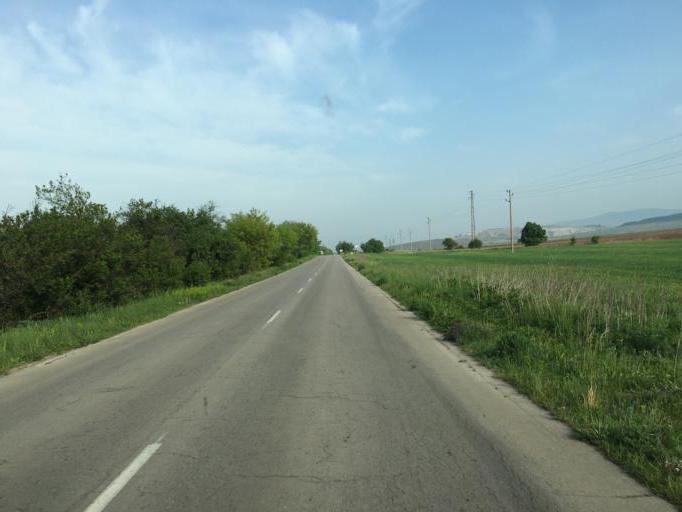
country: BG
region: Pernik
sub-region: Obshtina Radomir
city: Radomir
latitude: 42.4868
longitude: 23.0501
